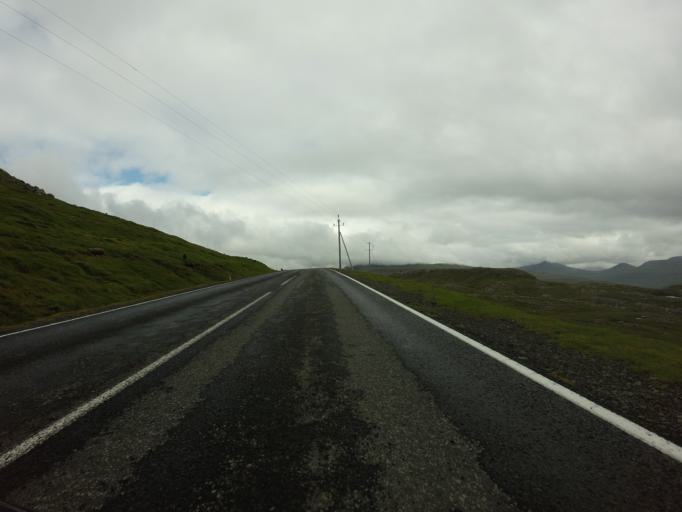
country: FO
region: Streymoy
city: Kollafjordhur
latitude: 62.0831
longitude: -6.9366
